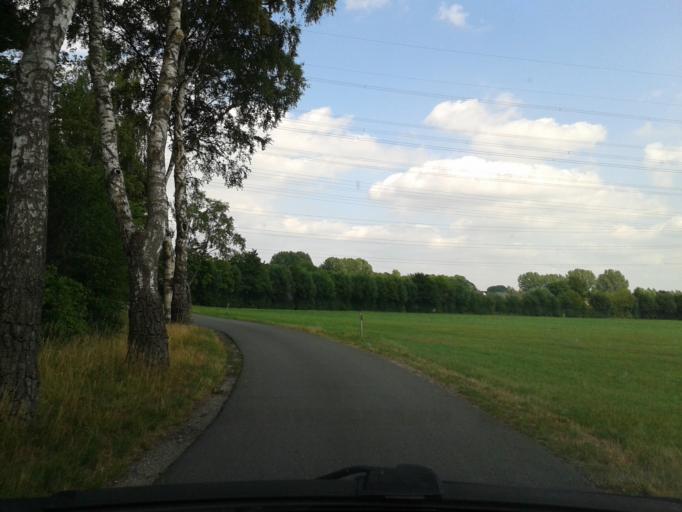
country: DE
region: North Rhine-Westphalia
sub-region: Regierungsbezirk Detmold
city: Paderborn
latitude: 51.7542
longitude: 8.6990
